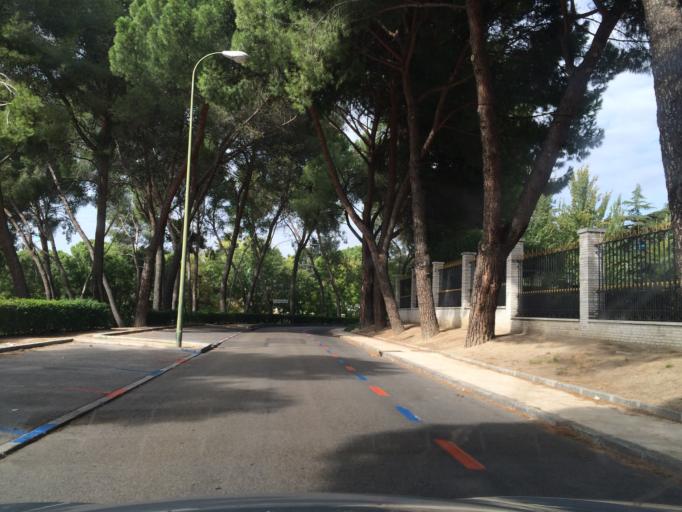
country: ES
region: Madrid
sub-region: Provincia de Madrid
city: Moncloa-Aravaca
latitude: 40.4265
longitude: -3.7225
